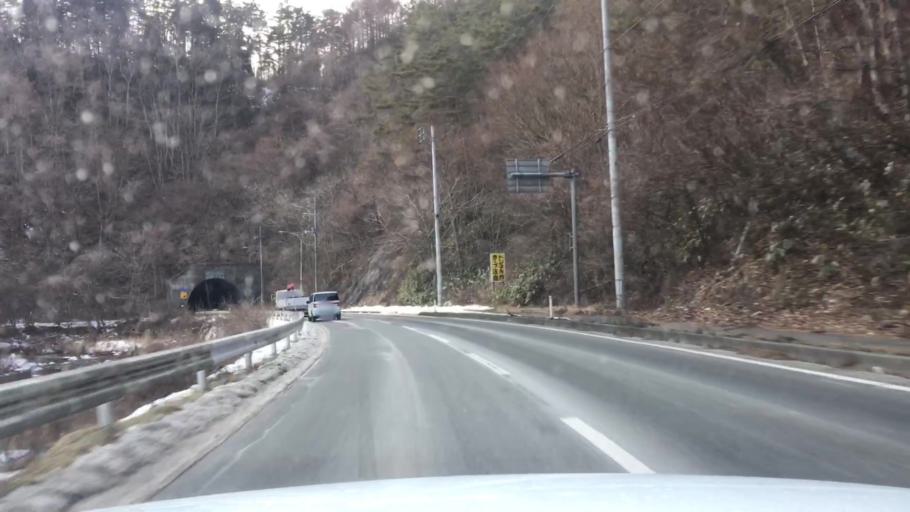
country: JP
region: Iwate
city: Morioka-shi
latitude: 39.6774
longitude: 141.2253
